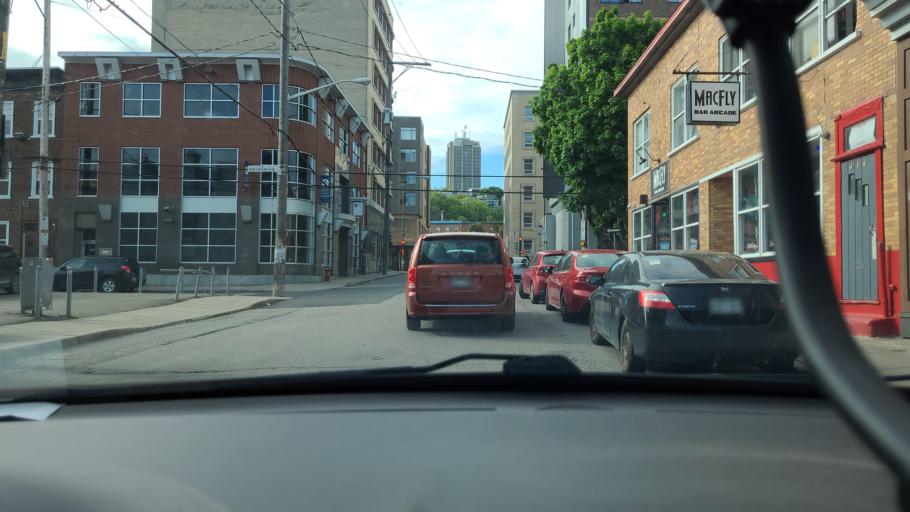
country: CA
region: Quebec
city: Quebec
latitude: 46.8129
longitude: -71.2284
